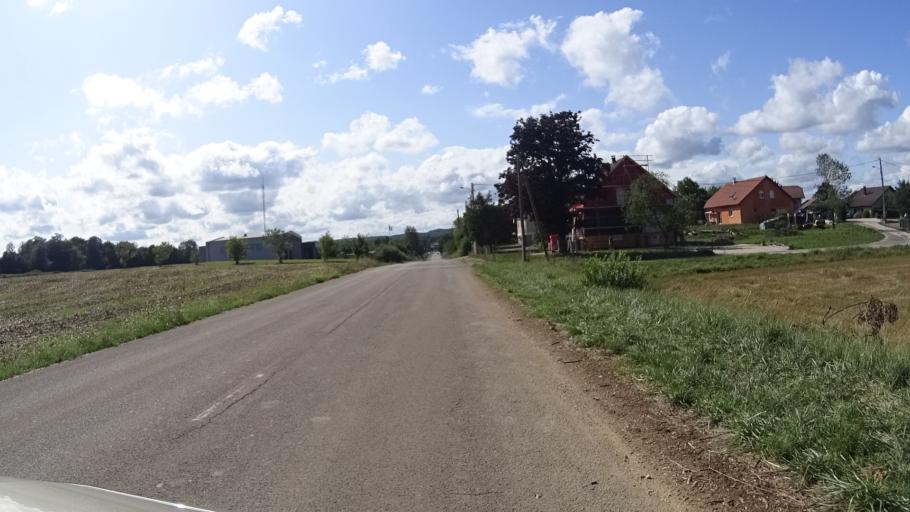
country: FR
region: Franche-Comte
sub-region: Departement du Doubs
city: Saone
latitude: 47.2077
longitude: 6.1093
